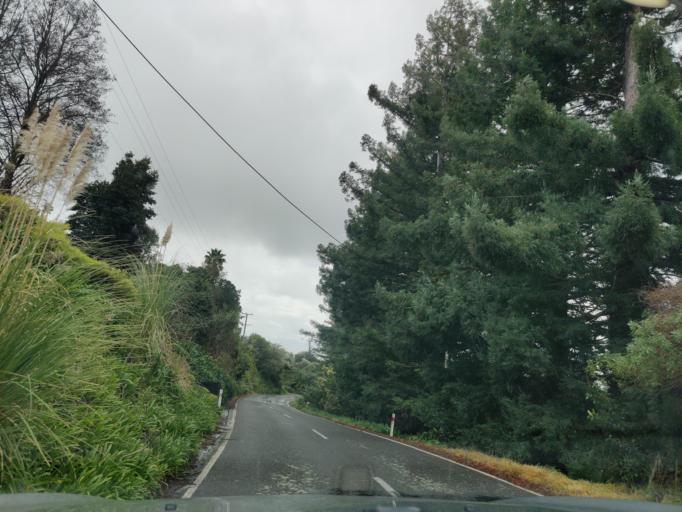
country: NZ
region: Hawke's Bay
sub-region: Hastings District
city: Hastings
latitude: -39.6827
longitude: 176.8980
